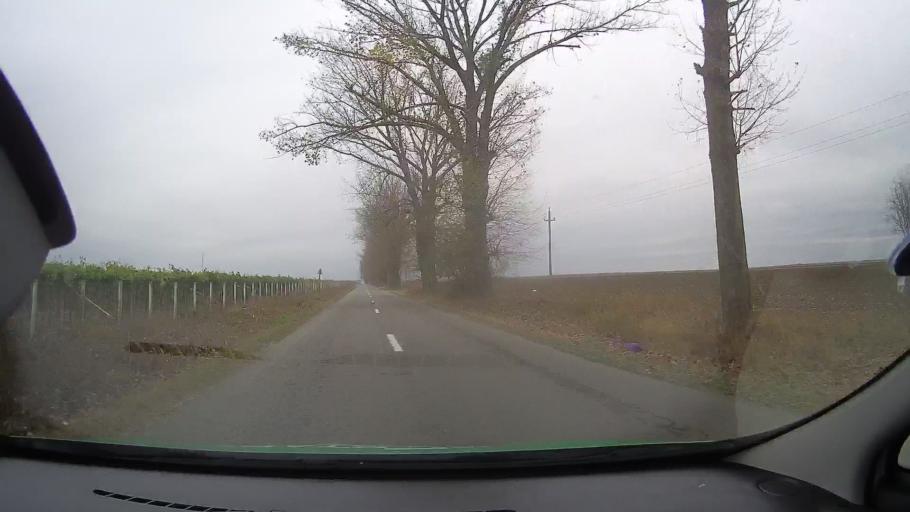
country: RO
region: Constanta
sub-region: Comuna Mihail Kogalniceanu
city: Mihail Kogalniceanu
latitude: 44.3838
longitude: 28.4613
